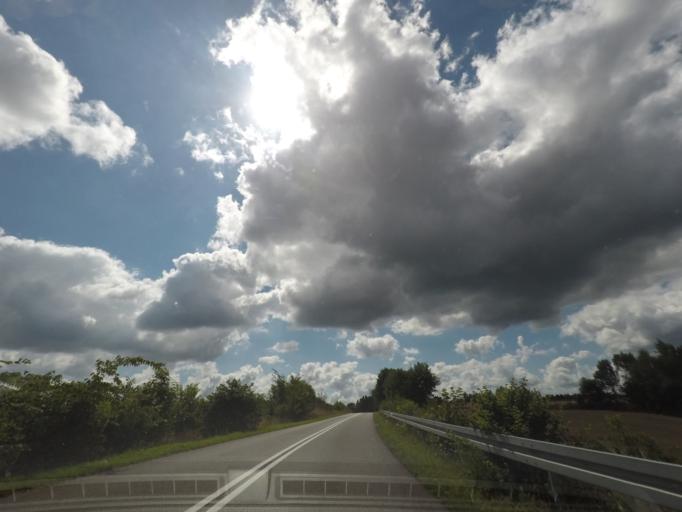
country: PL
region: Pomeranian Voivodeship
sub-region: Powiat wejherowski
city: Leczyce
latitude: 54.6005
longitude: 17.8436
